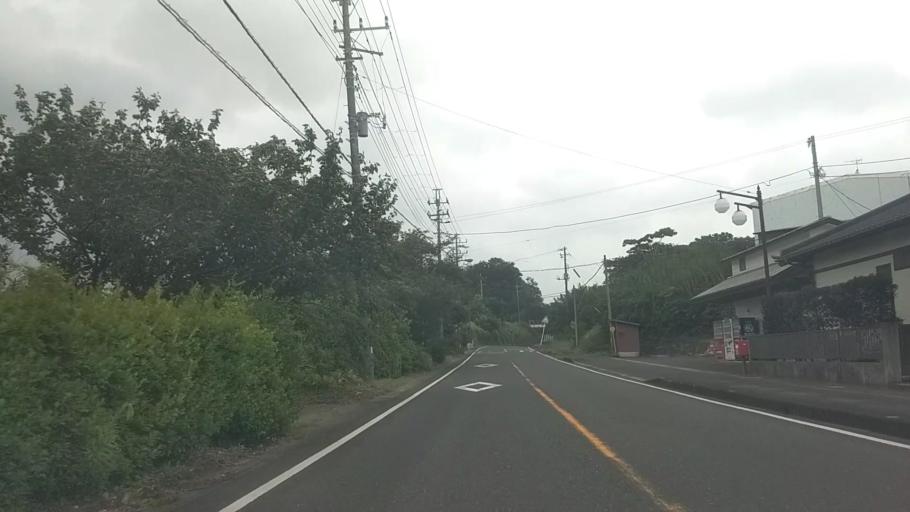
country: JP
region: Chiba
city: Kimitsu
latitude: 35.2201
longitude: 139.9076
